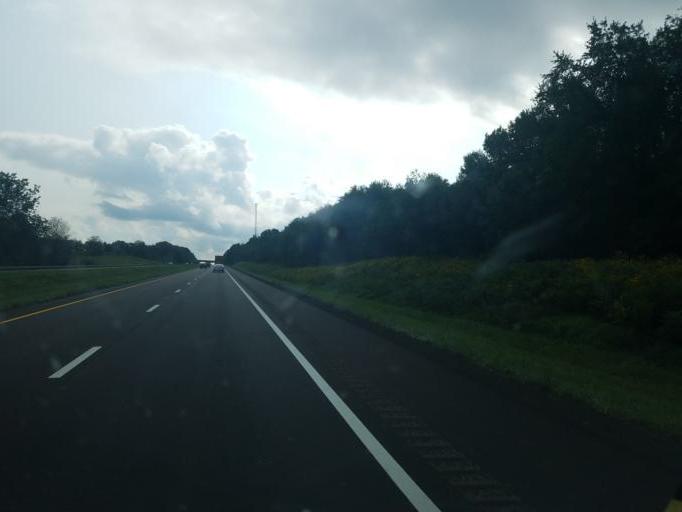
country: US
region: Ohio
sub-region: Wayne County
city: Shreve
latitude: 40.7839
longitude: -82.1462
